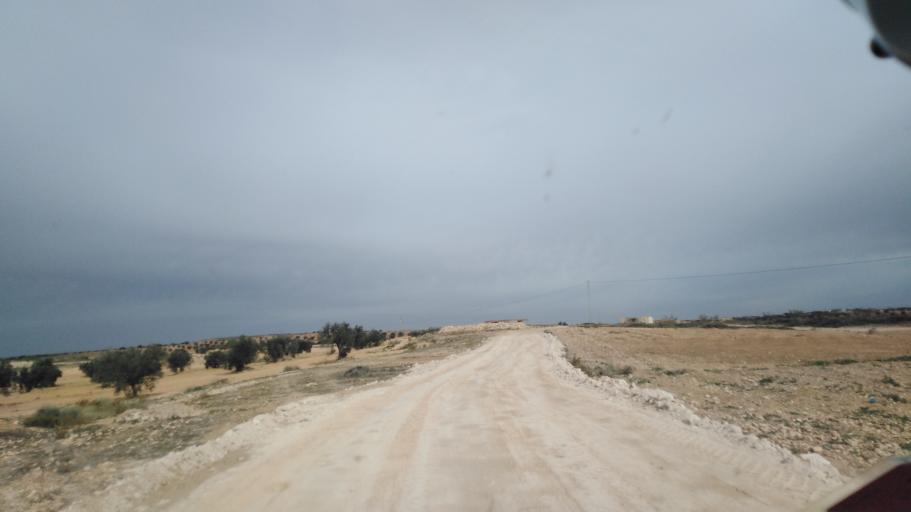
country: TN
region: Safaqis
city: Bi'r `Ali Bin Khalifah
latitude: 34.8162
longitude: 10.3072
